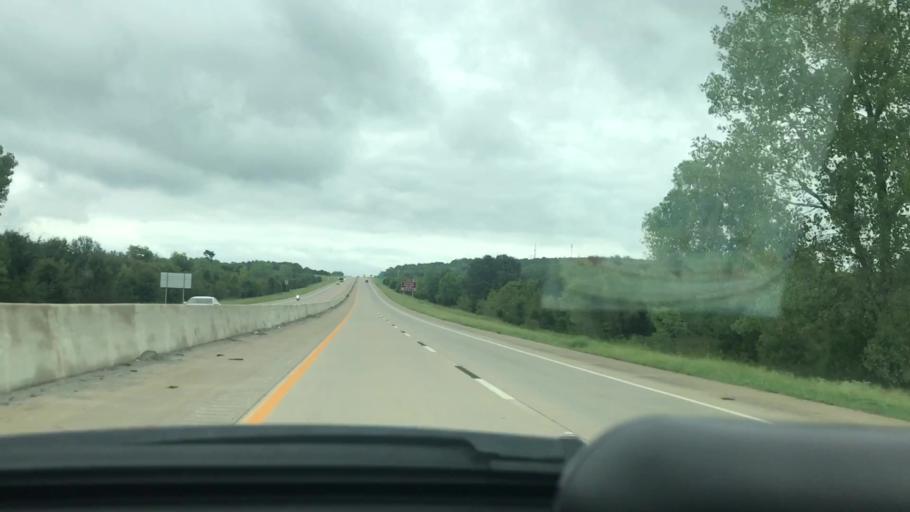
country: US
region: Oklahoma
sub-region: McIntosh County
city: Eufaula
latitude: 35.1617
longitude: -95.6550
